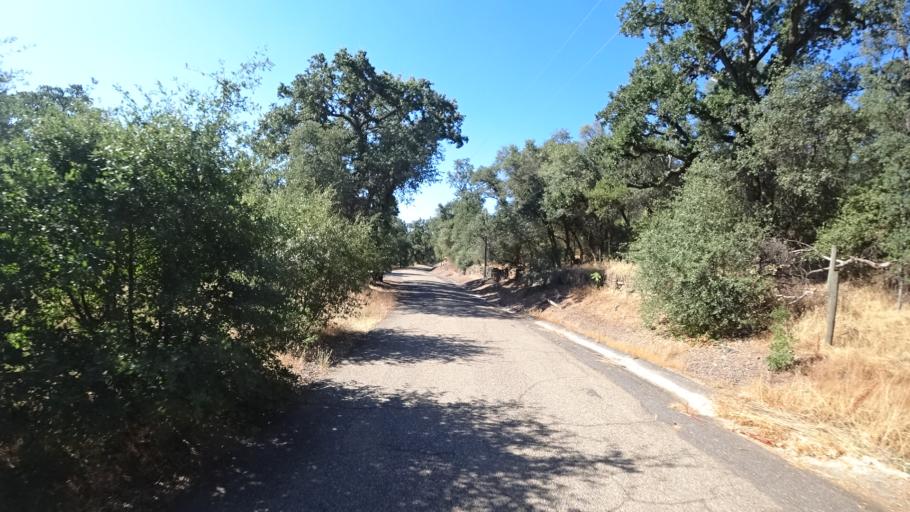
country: US
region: California
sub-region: Calaveras County
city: Murphys
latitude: 38.0984
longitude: -120.4700
